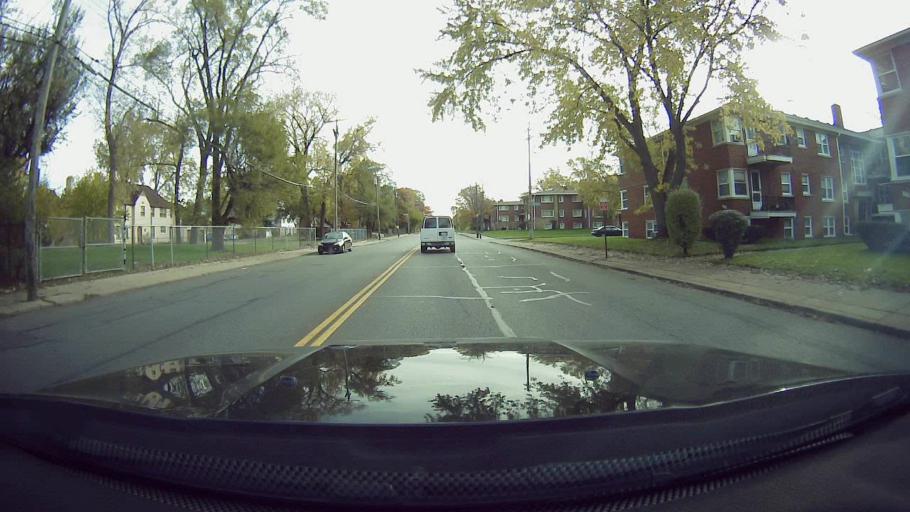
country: US
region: Michigan
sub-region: Wayne County
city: Highland Park
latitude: 42.4173
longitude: -83.1291
